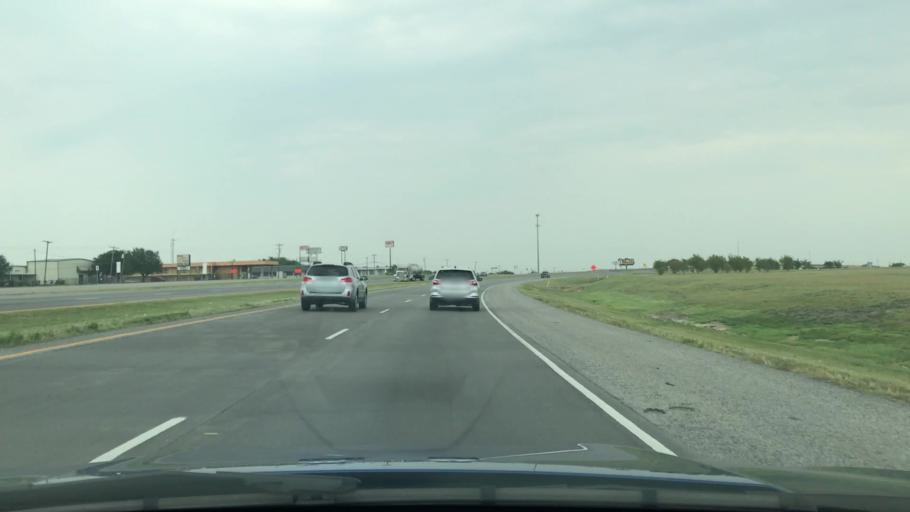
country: US
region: Texas
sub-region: Kaufman County
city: Talty
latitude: 32.7401
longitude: -96.3646
